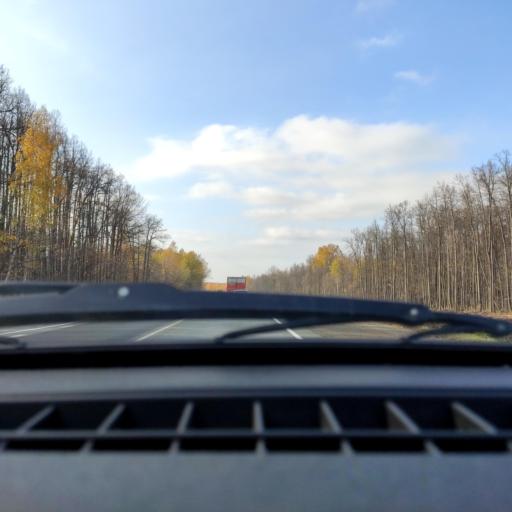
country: RU
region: Bashkortostan
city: Iglino
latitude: 54.7254
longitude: 56.2465
